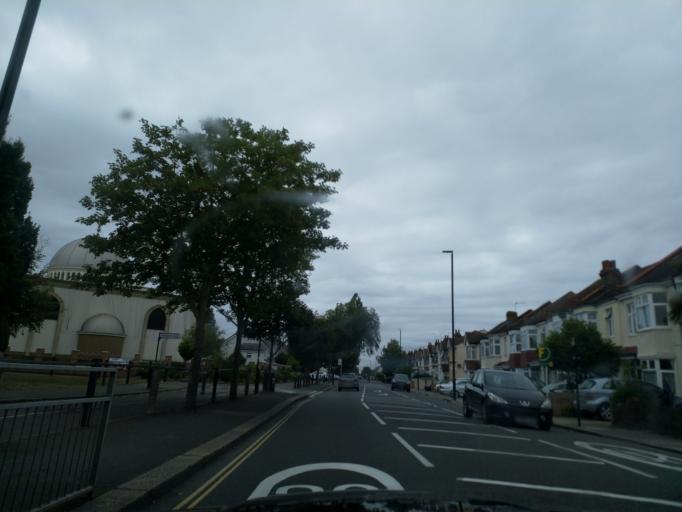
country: GB
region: England
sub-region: Greater London
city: Hounslow
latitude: 51.4589
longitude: -0.3739
